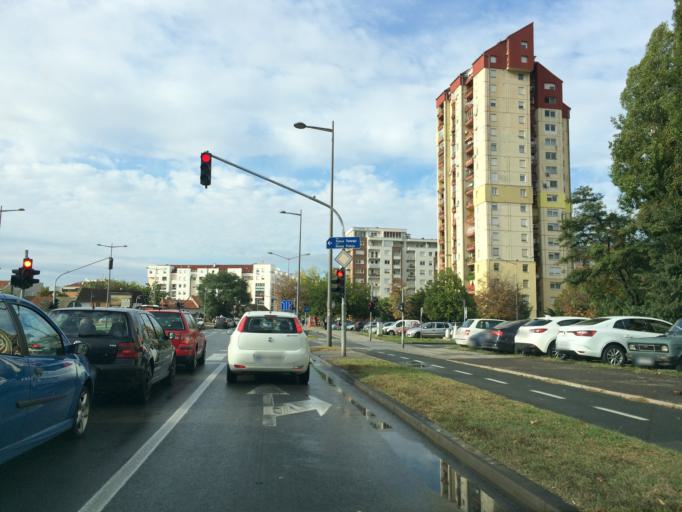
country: RS
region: Autonomna Pokrajina Vojvodina
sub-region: Juznobacki Okrug
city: Novi Sad
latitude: 45.2385
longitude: 19.8260
